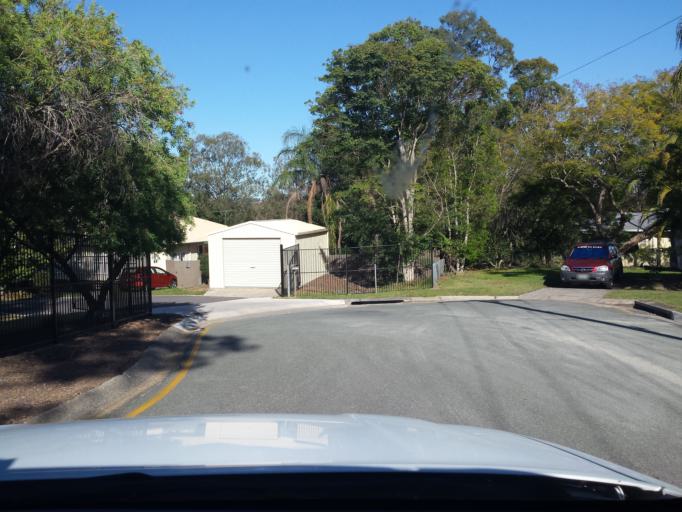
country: AU
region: Queensland
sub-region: Logan
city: Beenleigh
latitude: -27.7102
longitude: 153.1976
